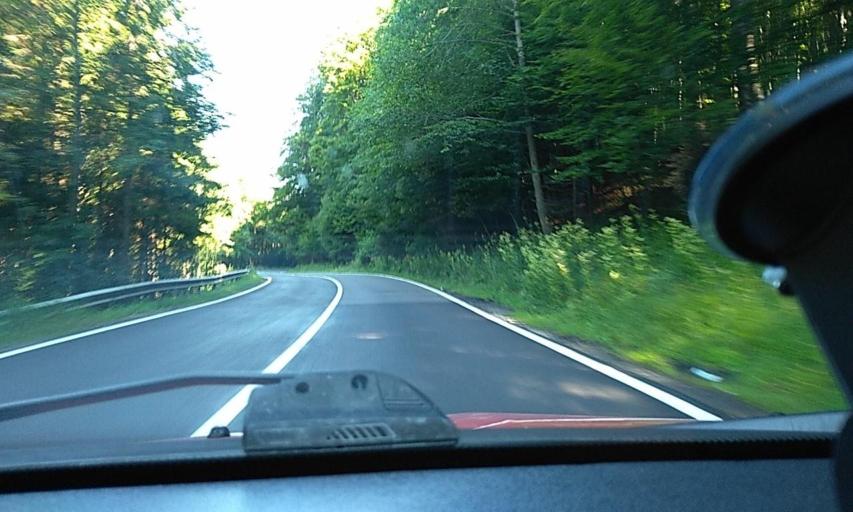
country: RO
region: Brasov
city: Crivina
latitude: 45.5030
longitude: 25.8547
